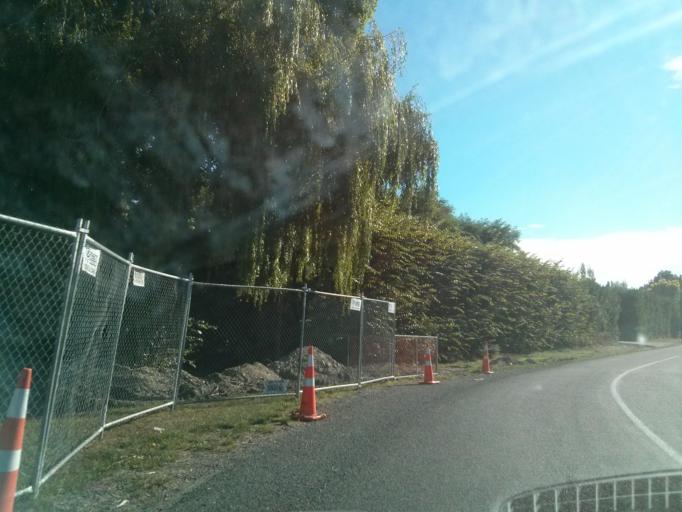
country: NZ
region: Canterbury
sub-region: Christchurch City
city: Christchurch
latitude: -43.4782
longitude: 172.5593
